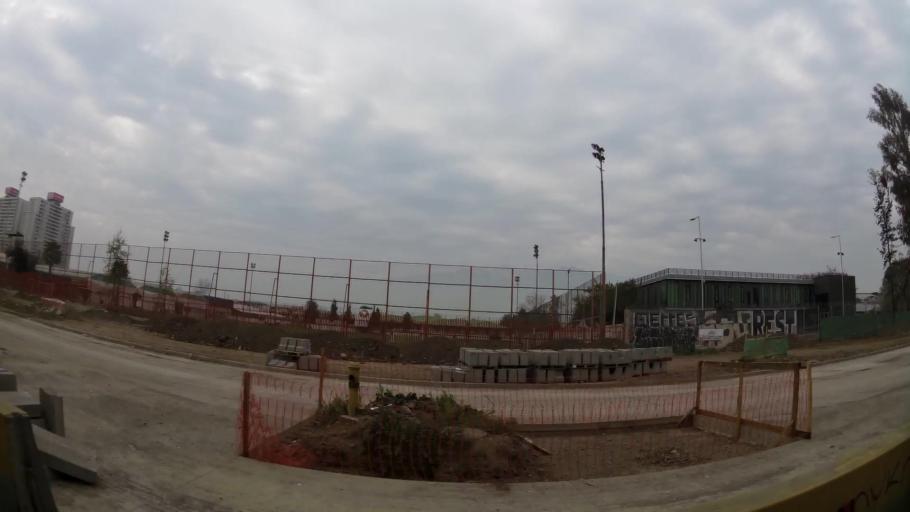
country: CL
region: Santiago Metropolitan
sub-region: Provincia de Santiago
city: Santiago
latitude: -33.4937
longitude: -70.6170
